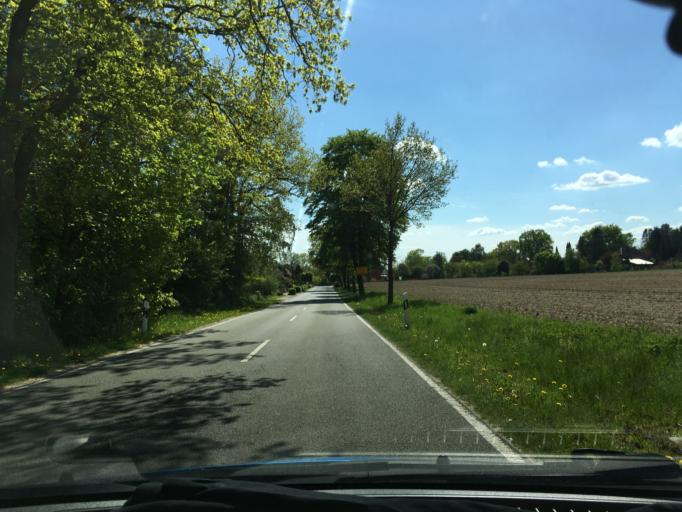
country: DE
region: Lower Saxony
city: Zernien
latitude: 53.0528
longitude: 10.8795
